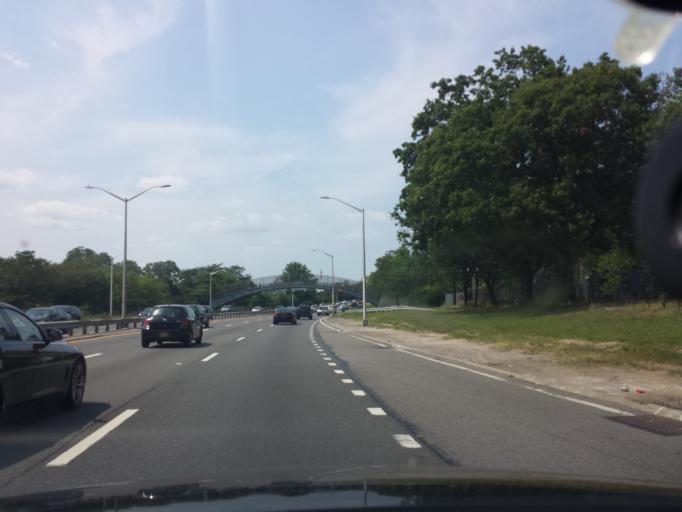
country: US
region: New York
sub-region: Kings County
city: Coney Island
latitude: 40.5865
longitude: -73.9908
